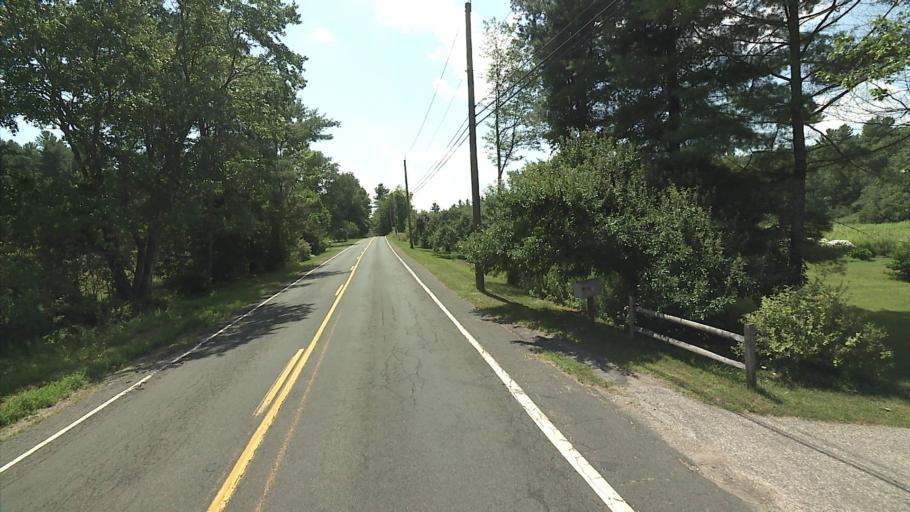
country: US
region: Connecticut
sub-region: Litchfield County
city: Canaan
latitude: 41.8811
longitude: -73.2887
